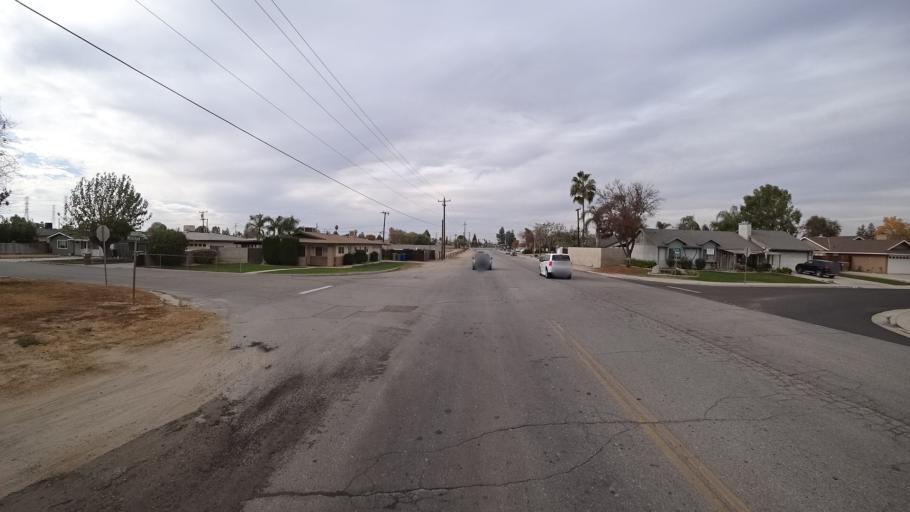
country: US
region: California
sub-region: Kern County
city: Greenacres
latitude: 35.3907
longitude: -119.1249
